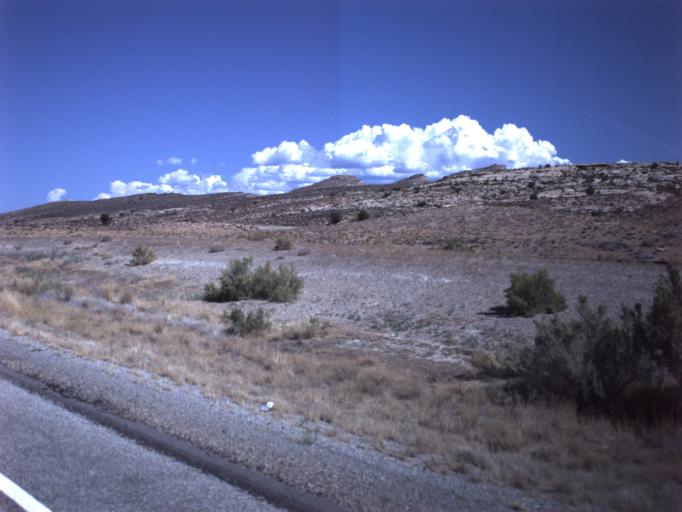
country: US
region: Utah
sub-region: Grand County
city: Moab
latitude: 38.8530
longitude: -109.8023
